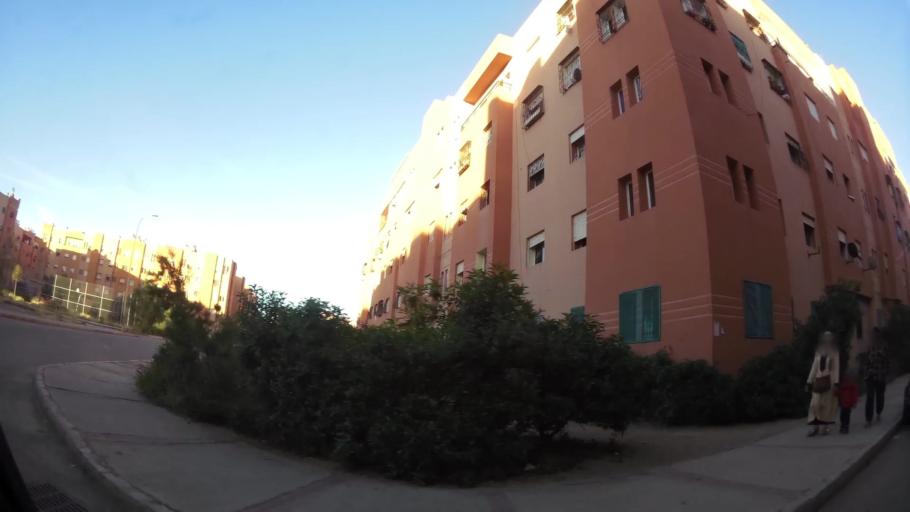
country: MA
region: Marrakech-Tensift-Al Haouz
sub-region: Marrakech
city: Marrakesh
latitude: 31.7483
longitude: -8.1192
